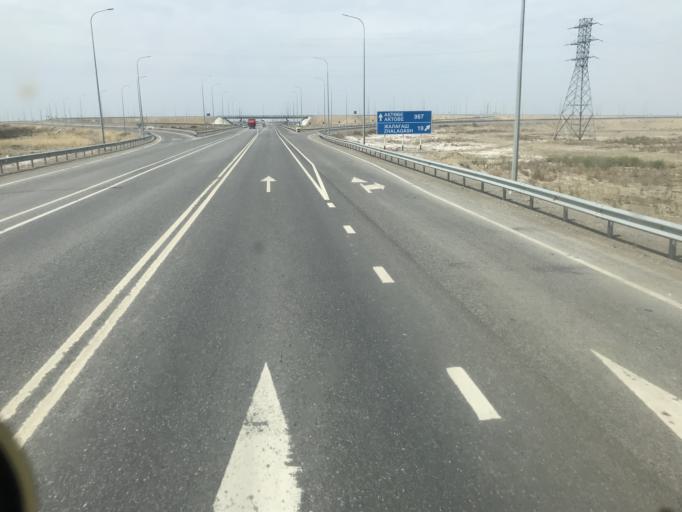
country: KZ
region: Qyzylorda
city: Dzhalagash
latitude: 44.9892
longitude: 64.5315
